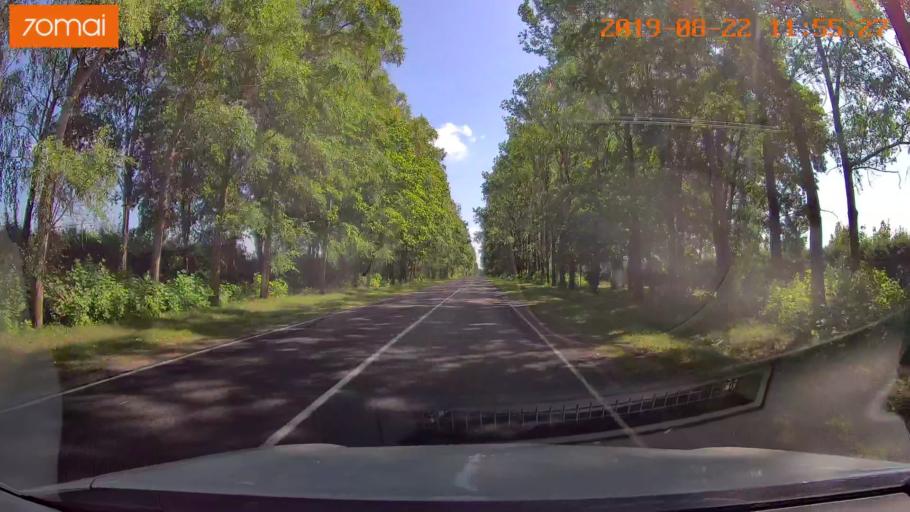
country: BY
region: Minsk
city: Prawdzinski
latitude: 53.4315
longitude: 27.5480
